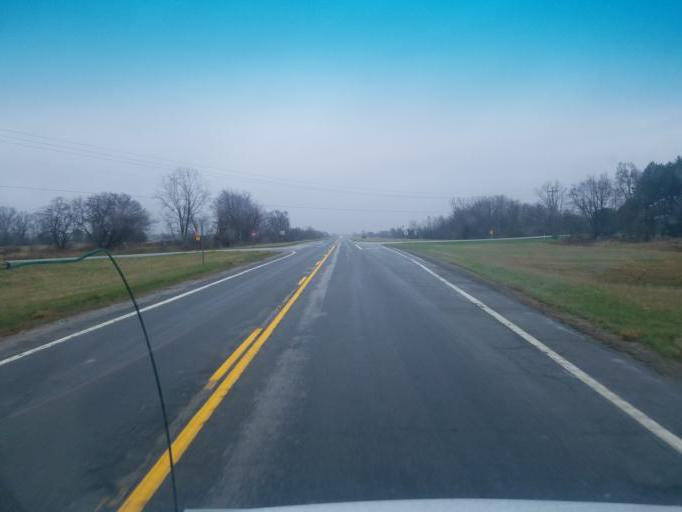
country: US
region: Ohio
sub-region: Wood County
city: Bowling Green
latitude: 41.3692
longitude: -83.7094
